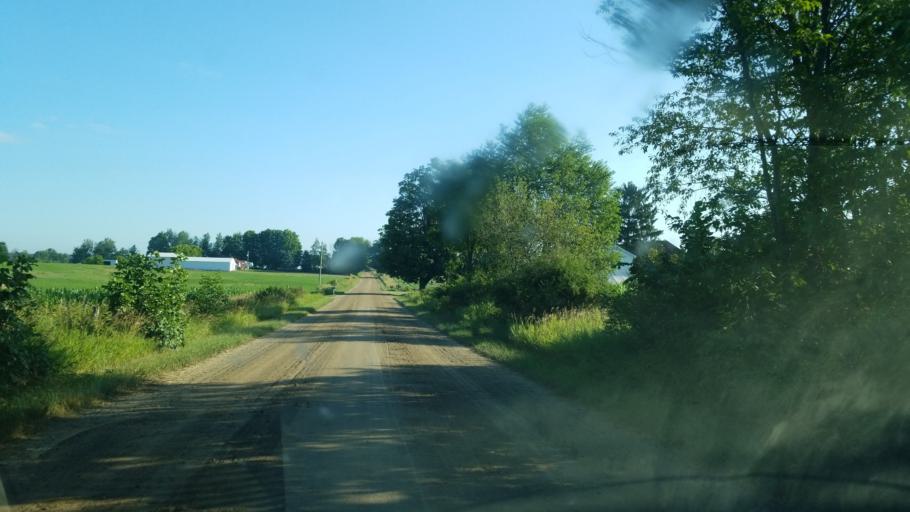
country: US
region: Michigan
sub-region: Mecosta County
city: Canadian Lakes
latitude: 43.5487
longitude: -85.3632
